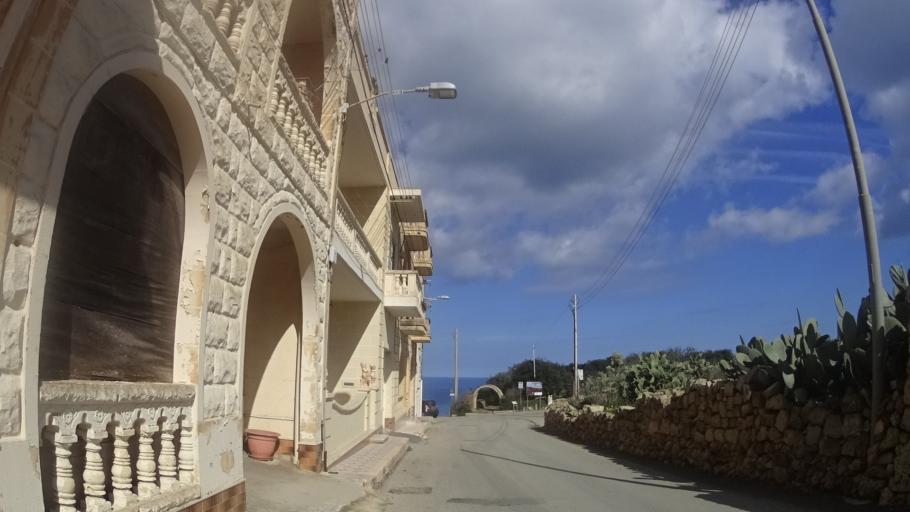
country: MT
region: In-Nadur
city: Nadur
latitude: 36.0511
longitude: 14.3004
